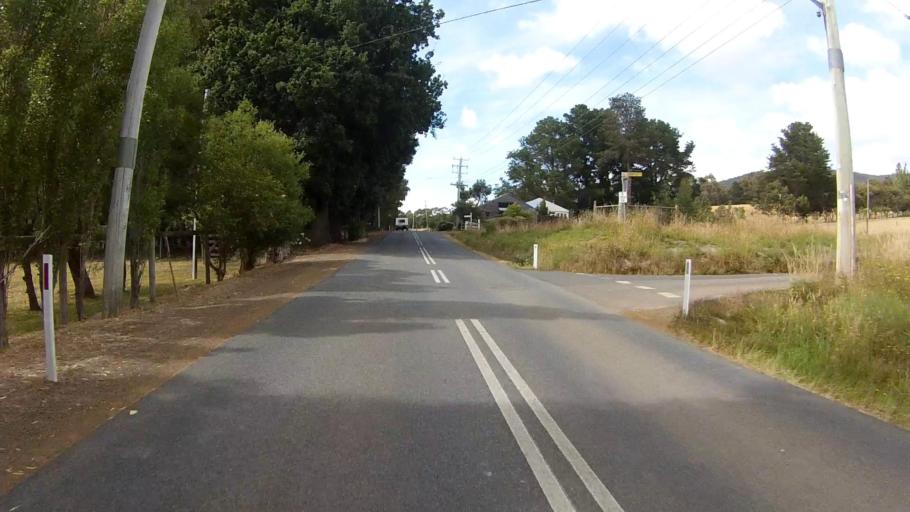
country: AU
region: Tasmania
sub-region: Kingborough
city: Kettering
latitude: -43.1765
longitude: 147.2362
